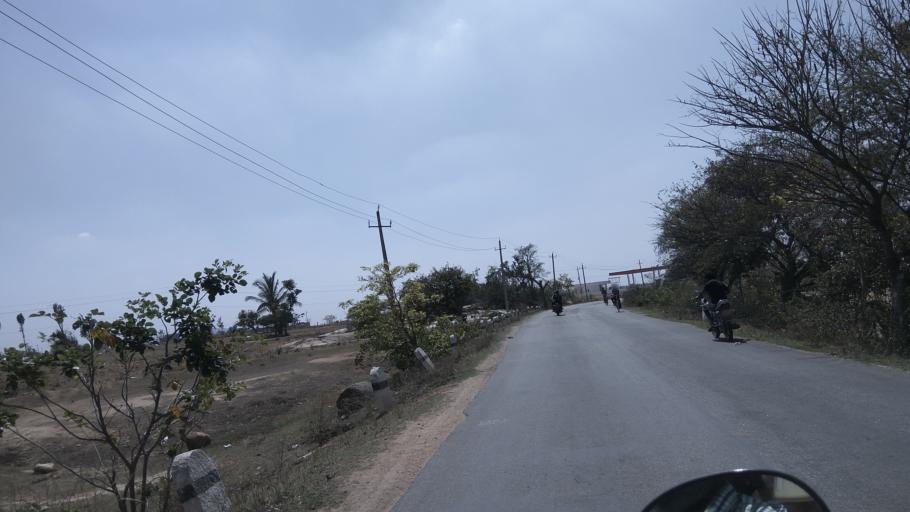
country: IN
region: Karnataka
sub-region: Kolar
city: Mulbagal
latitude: 13.1654
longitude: 78.3722
